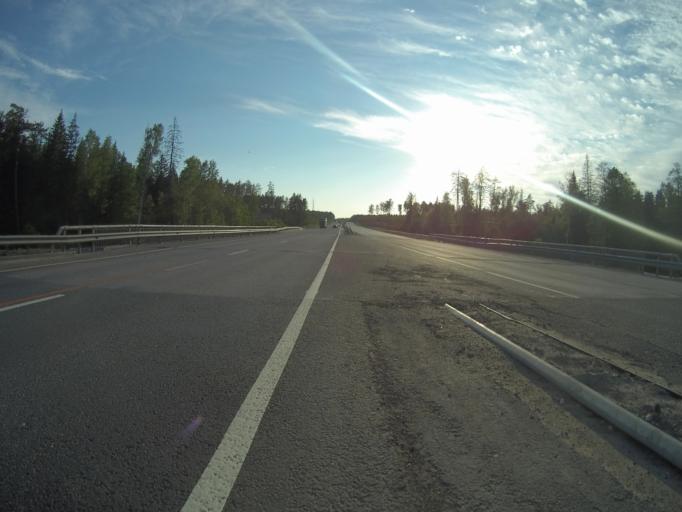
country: RU
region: Vladimir
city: Orgtrud
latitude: 56.1037
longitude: 40.6591
